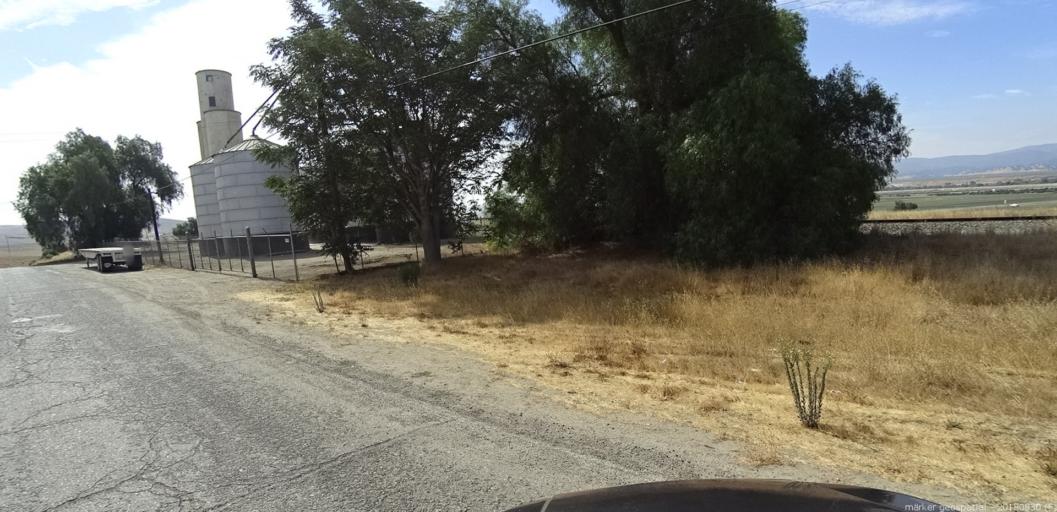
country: US
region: California
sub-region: Monterey County
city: King City
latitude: 36.1284
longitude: -121.0174
